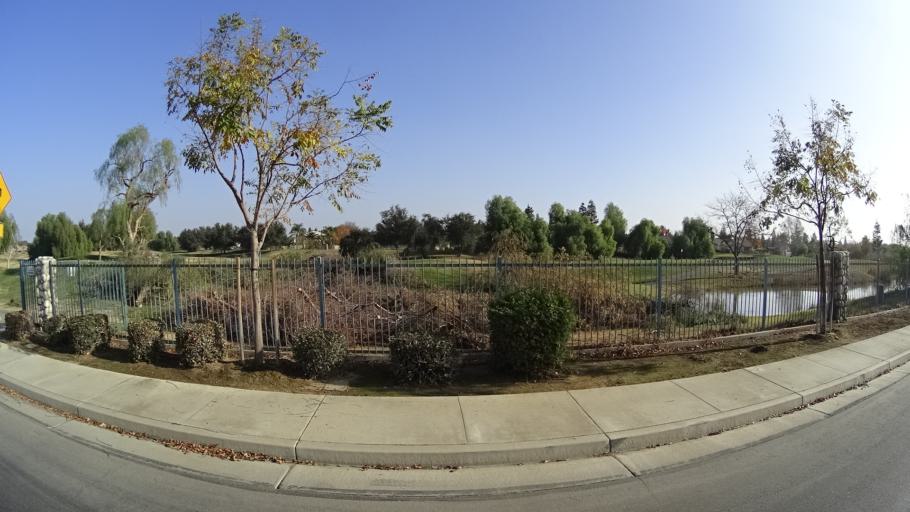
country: US
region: California
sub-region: Kern County
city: Greenacres
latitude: 35.4170
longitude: -119.1020
